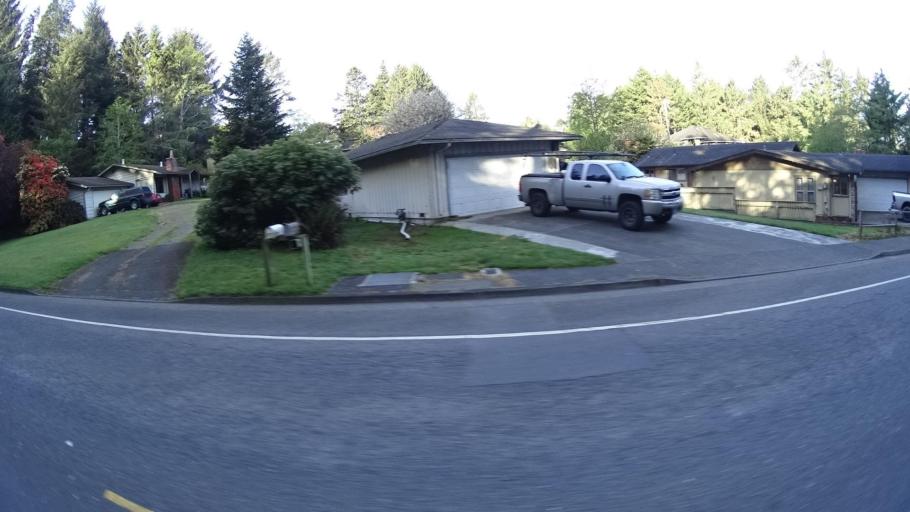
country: US
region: California
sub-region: Humboldt County
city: Humboldt Hill
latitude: 40.7260
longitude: -124.2021
